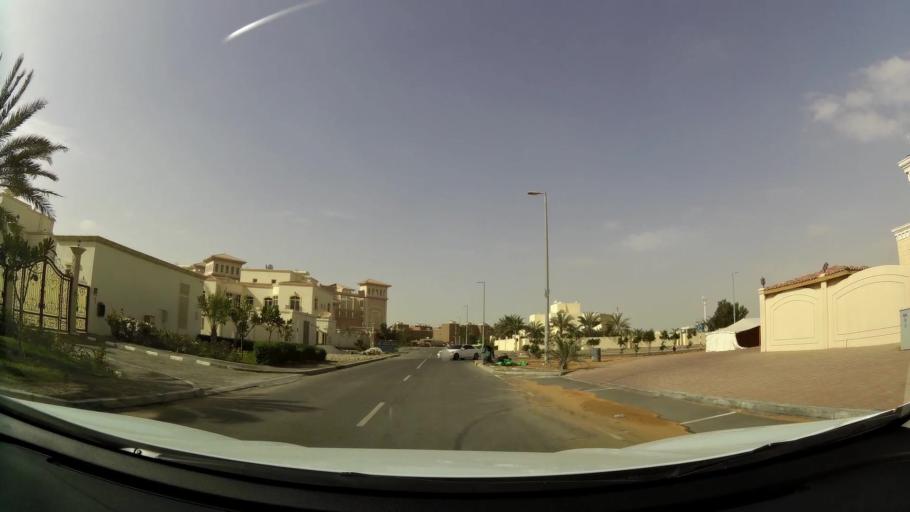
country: AE
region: Abu Dhabi
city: Abu Dhabi
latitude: 24.4298
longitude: 54.5985
